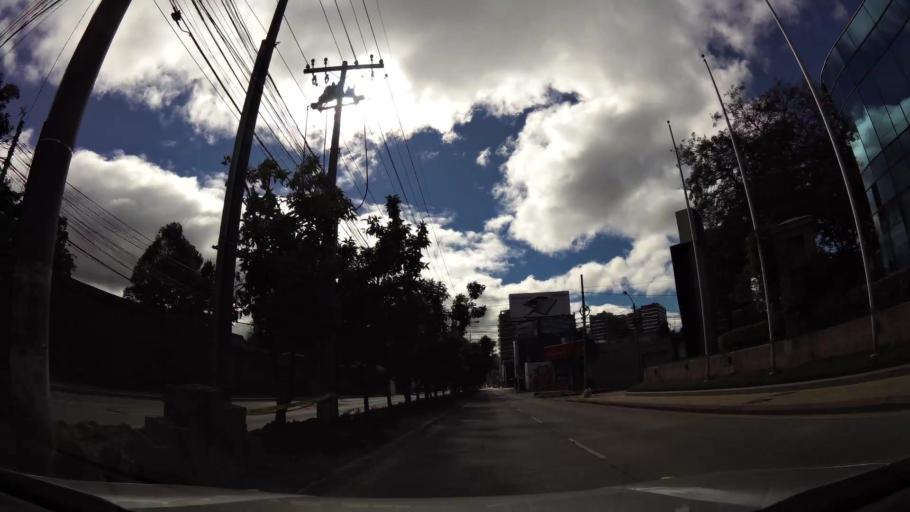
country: GT
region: Guatemala
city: Santa Catarina Pinula
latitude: 14.6017
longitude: -90.5097
